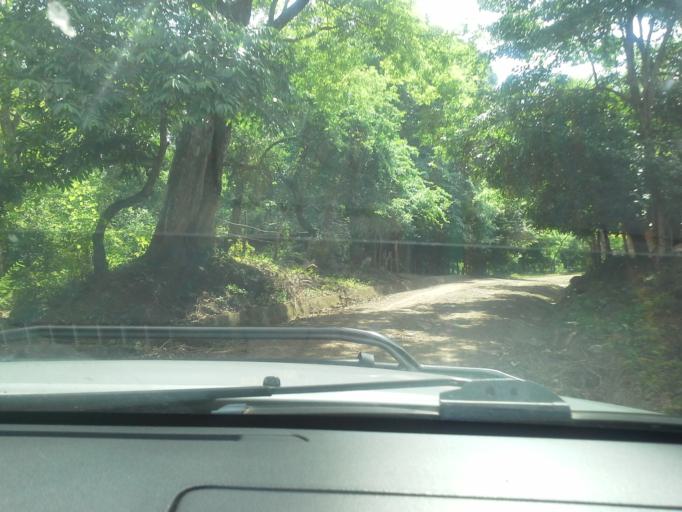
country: NI
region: Matagalpa
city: Terrabona
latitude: 12.7039
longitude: -85.9468
